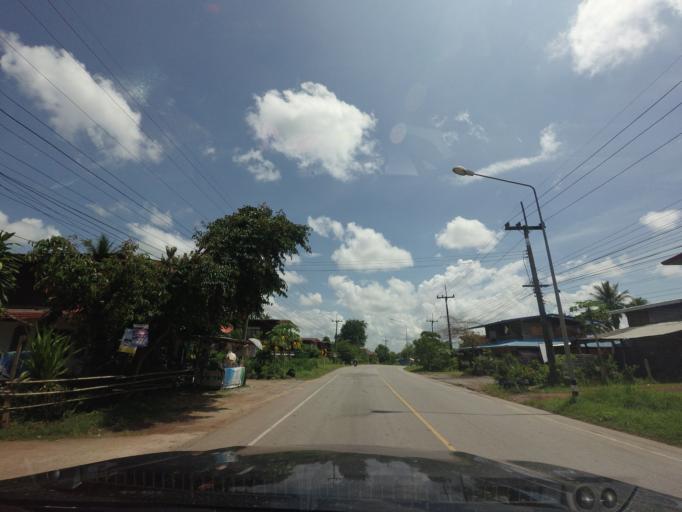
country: TH
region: Nong Khai
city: Pho Tak
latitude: 17.7804
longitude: 102.3852
